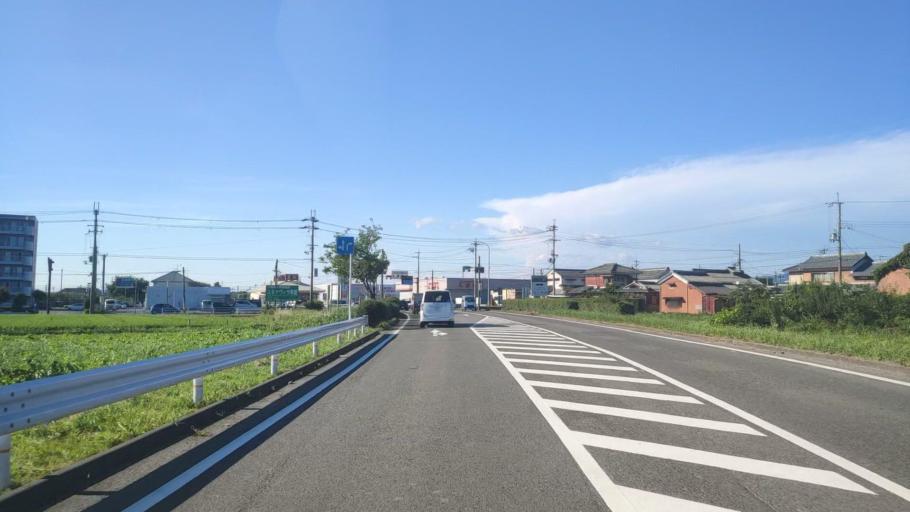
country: JP
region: Shiga Prefecture
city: Hino
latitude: 35.0106
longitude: 136.2402
